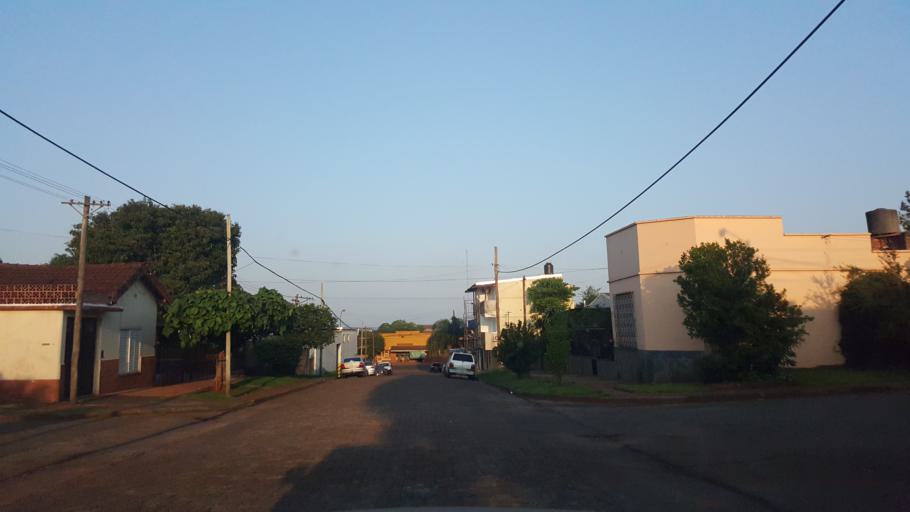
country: AR
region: Misiones
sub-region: Departamento de Capital
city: Posadas
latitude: -27.3961
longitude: -55.9029
